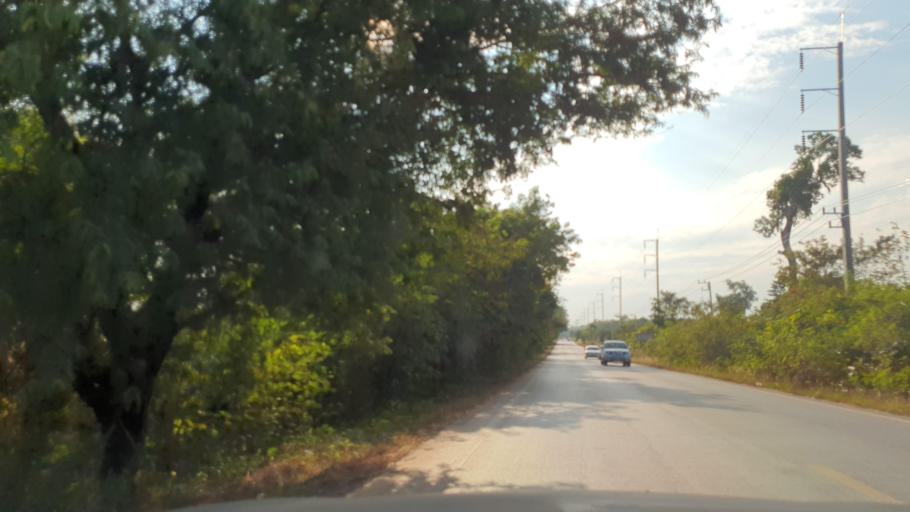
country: TH
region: Nong Khai
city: Bueng Khong Long
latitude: 18.0247
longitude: 104.1195
